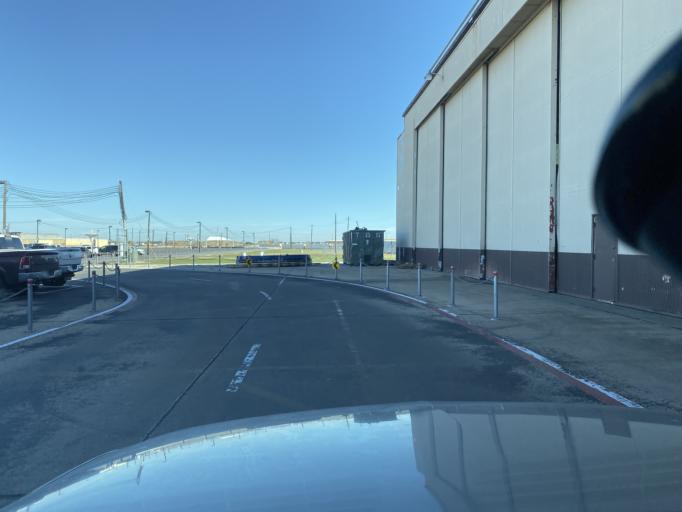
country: US
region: Texas
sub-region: Travis County
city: Hornsby Bend
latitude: 30.1936
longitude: -97.6682
